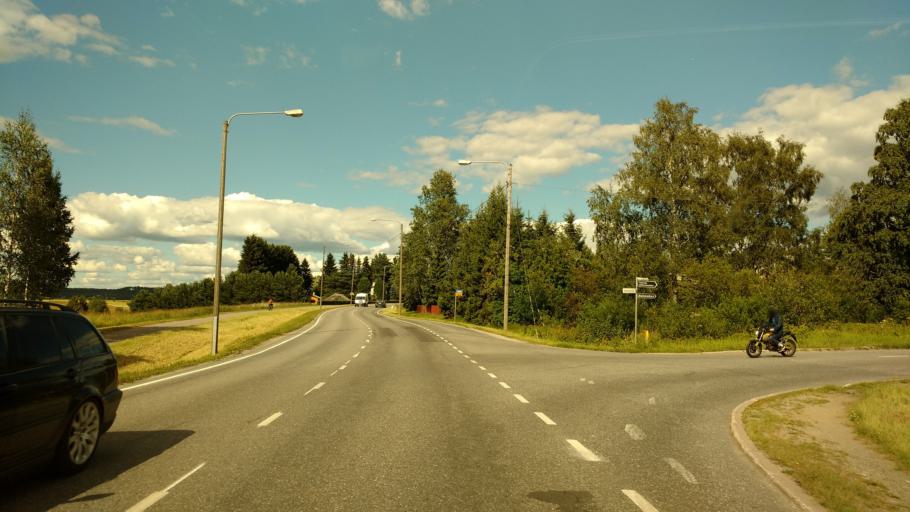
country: FI
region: Varsinais-Suomi
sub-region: Salo
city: Salo
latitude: 60.3993
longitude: 23.1592
